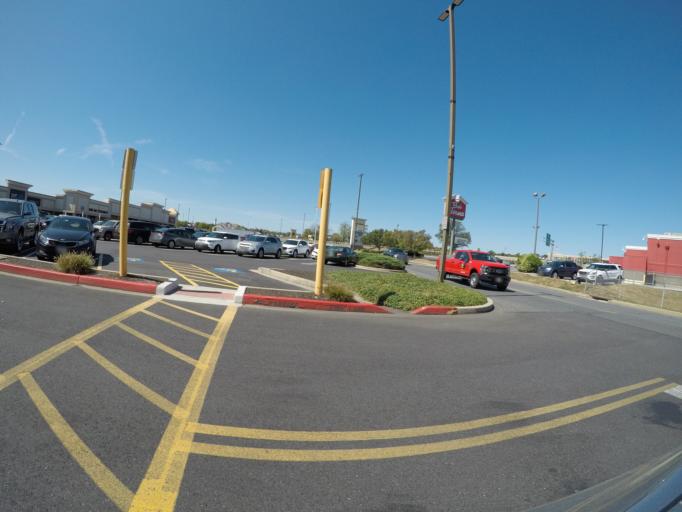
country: US
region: Maryland
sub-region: Harford County
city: Aberdeen
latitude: 39.5216
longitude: -76.1802
